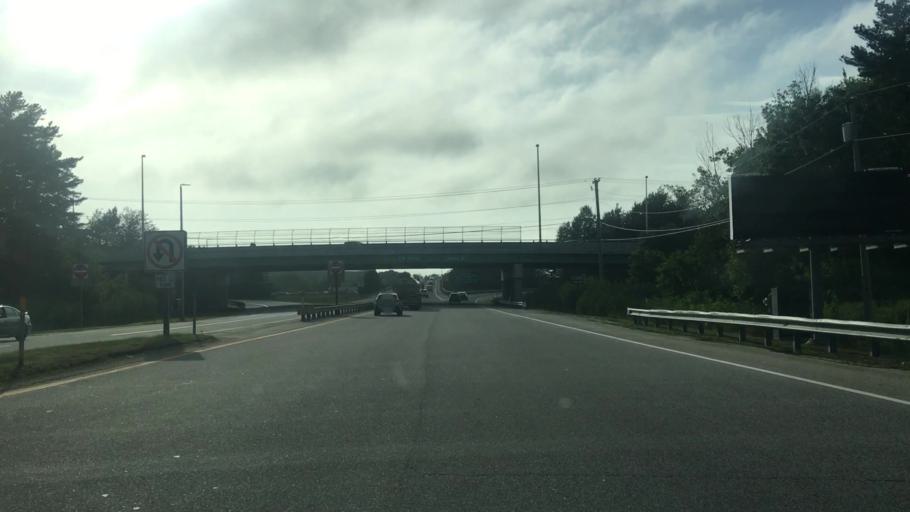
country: US
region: Maine
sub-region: Cumberland County
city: South Portland Gardens
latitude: 43.6305
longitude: -70.3394
